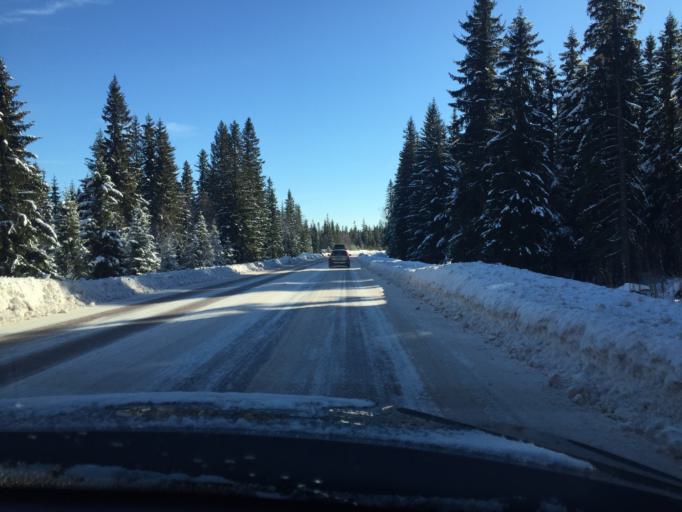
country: SE
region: Dalarna
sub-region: Malung-Saelens kommun
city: Malung
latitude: 61.1693
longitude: 13.1840
